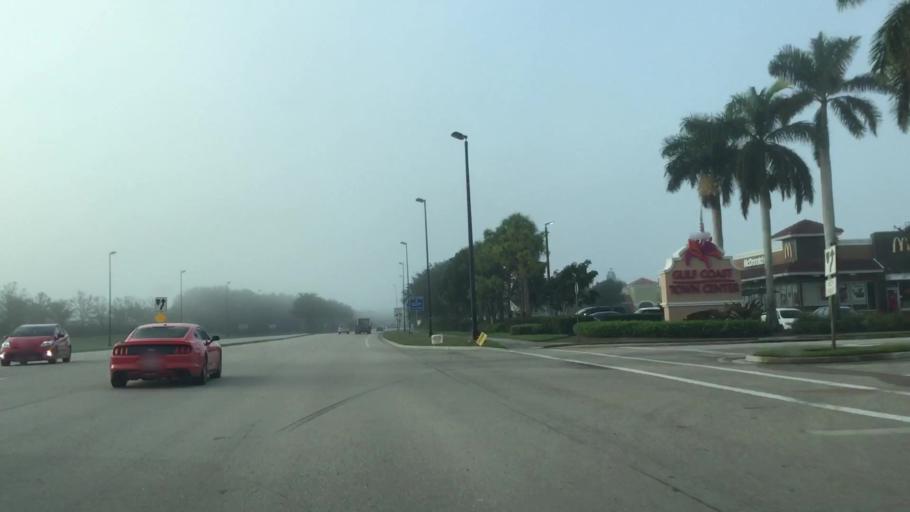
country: US
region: Florida
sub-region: Lee County
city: Three Oaks
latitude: 26.4855
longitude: -81.7845
